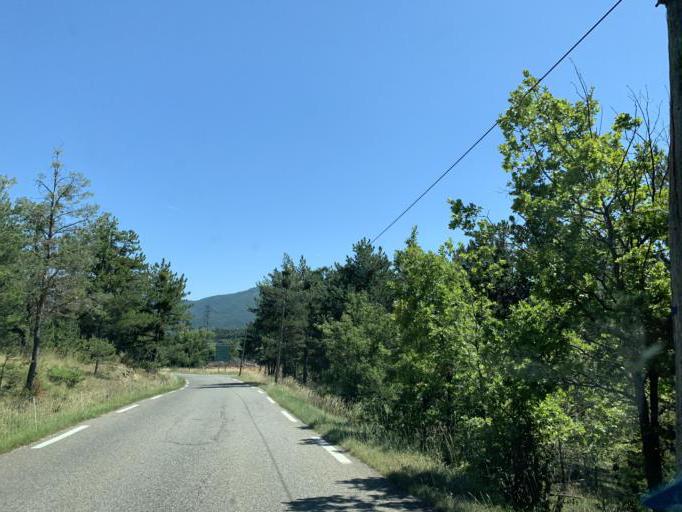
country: FR
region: Provence-Alpes-Cote d'Azur
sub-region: Departement des Hautes-Alpes
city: La Batie-Neuve
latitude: 44.5766
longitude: 6.1797
